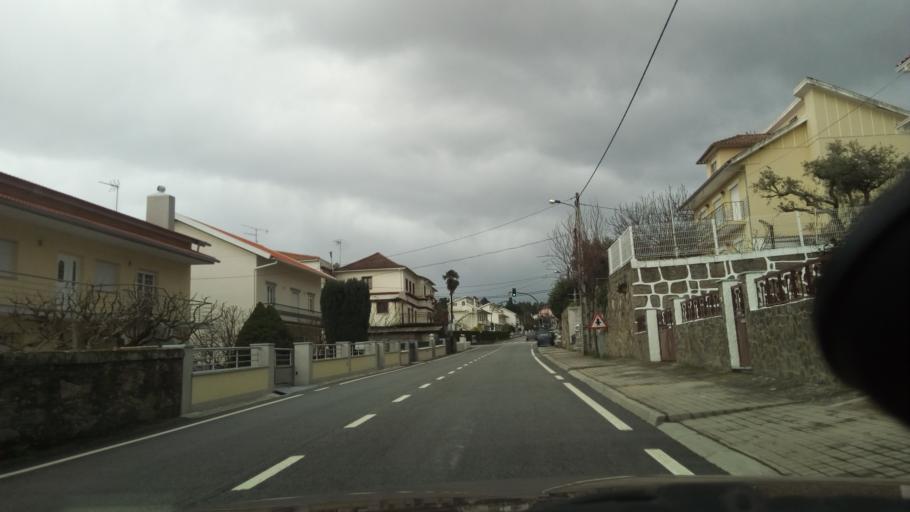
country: PT
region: Guarda
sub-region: Manteigas
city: Manteigas
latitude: 40.5144
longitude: -7.5832
